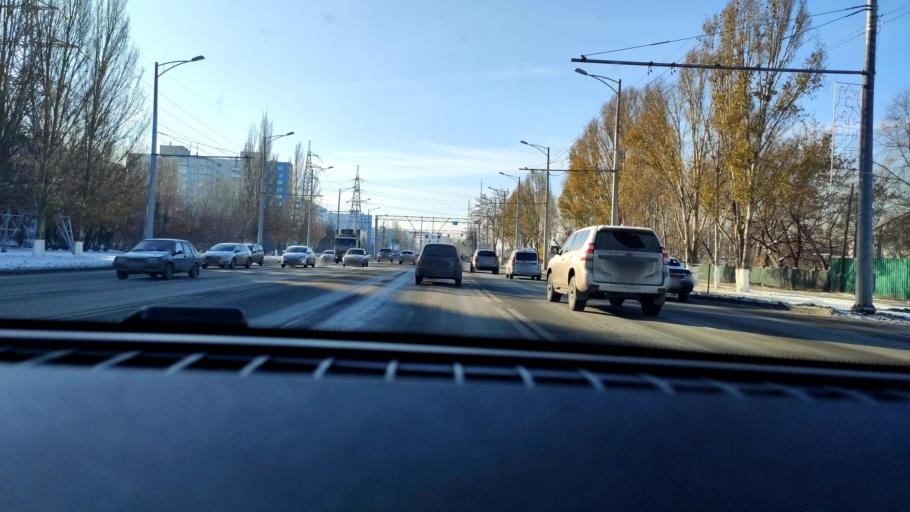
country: RU
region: Samara
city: Samara
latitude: 53.2430
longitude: 50.2087
